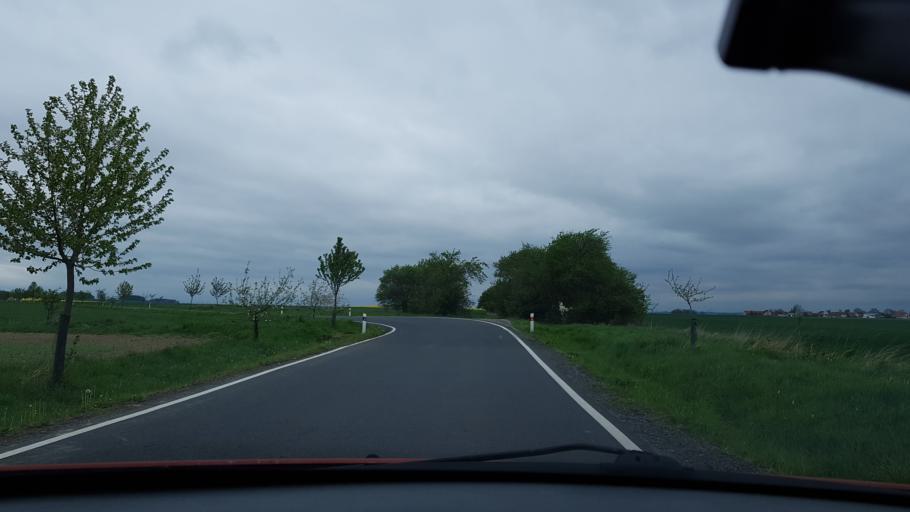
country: CZ
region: Olomoucky
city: Vidnava
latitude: 50.3768
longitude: 17.1738
